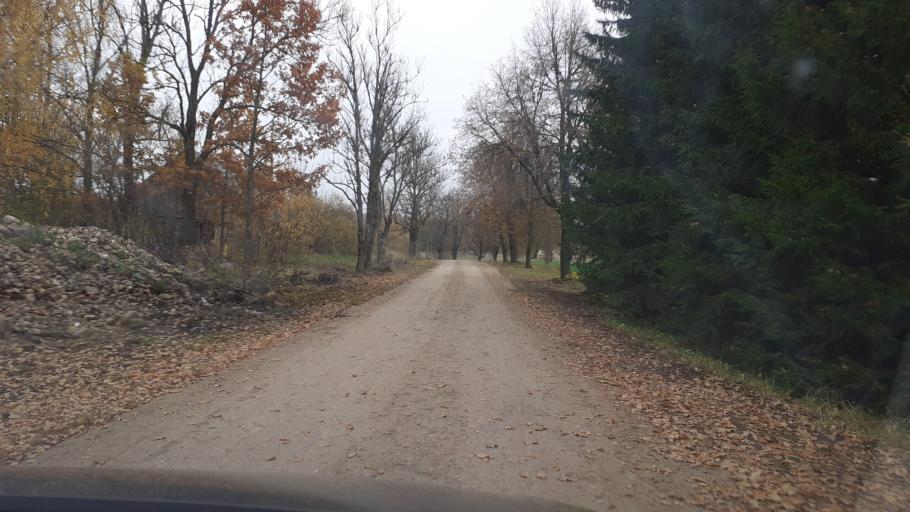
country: LV
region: Skrunda
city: Skrunda
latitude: 56.8569
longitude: 22.2246
